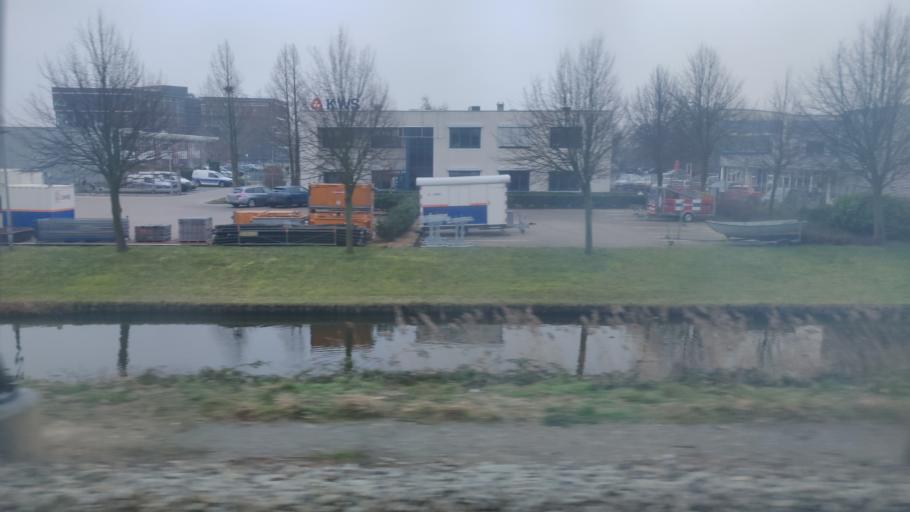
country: NL
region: North Holland
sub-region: Gemeente Langedijk
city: Broek op Langedijk
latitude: 52.6678
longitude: 4.8181
